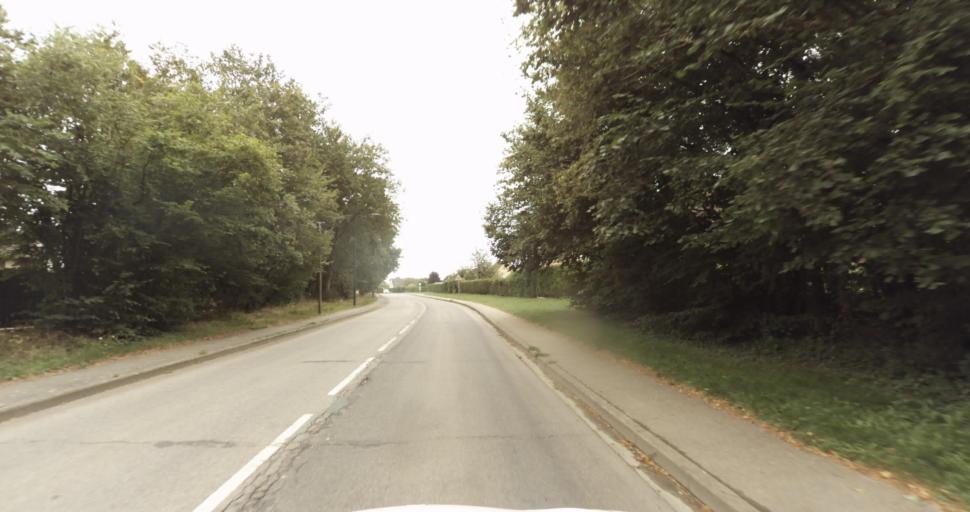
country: FR
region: Haute-Normandie
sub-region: Departement de l'Eure
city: Gravigny
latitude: 49.0333
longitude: 1.1773
